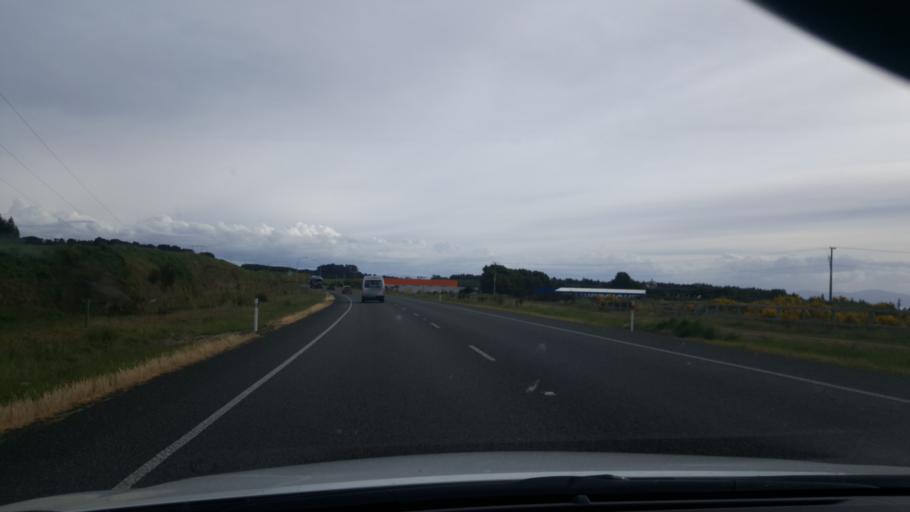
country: NZ
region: Waikato
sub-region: Taupo District
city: Taupo
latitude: -38.6989
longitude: 176.1123
